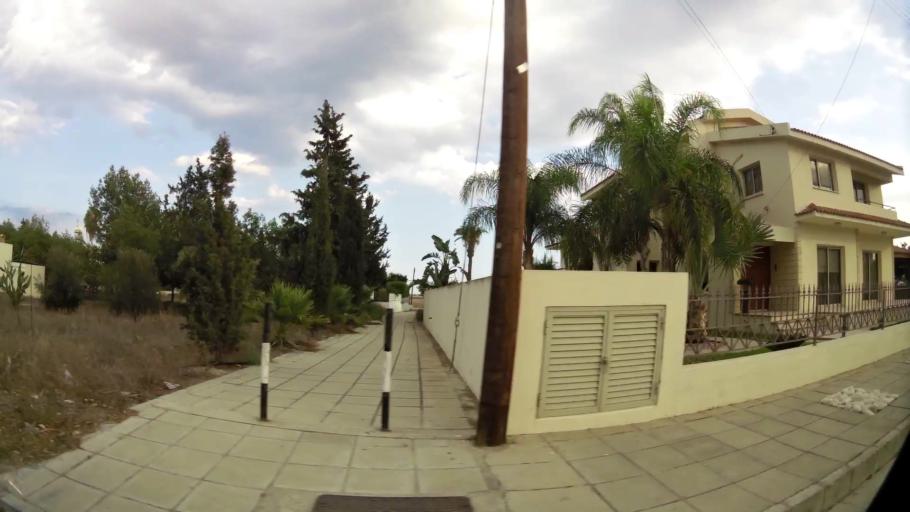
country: CY
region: Larnaka
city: Meneou
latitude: 34.8631
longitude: 33.5957
